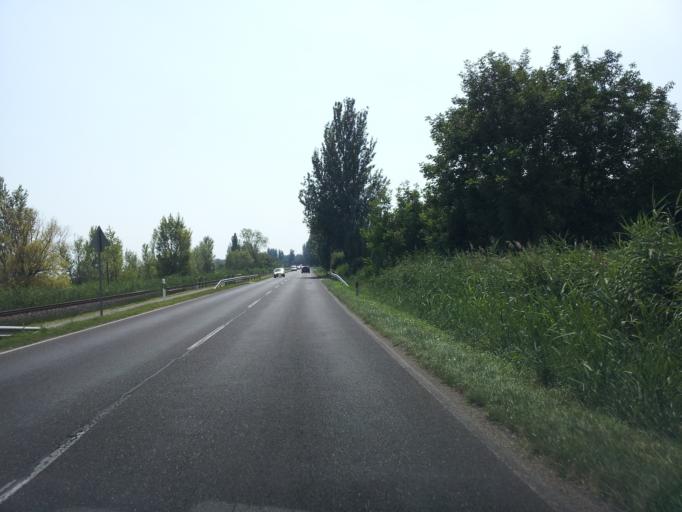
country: HU
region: Veszprem
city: Balatonalmadi
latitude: 46.9977
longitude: 17.9939
